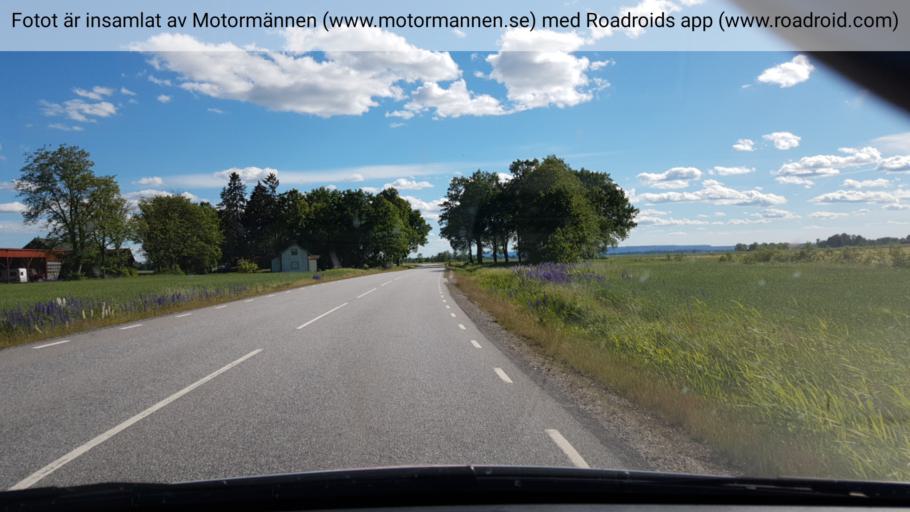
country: SE
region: Vaestra Goetaland
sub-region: Toreboda Kommun
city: Toereboda
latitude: 58.6193
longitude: 14.0133
